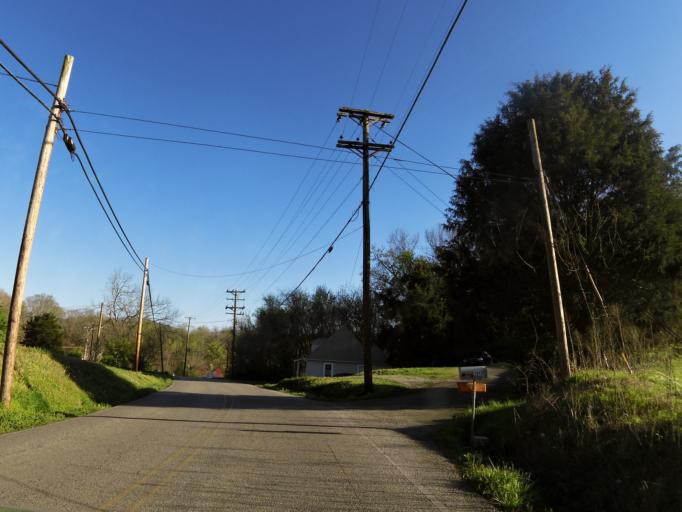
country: US
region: Tennessee
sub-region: Knox County
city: Knoxville
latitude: 35.9750
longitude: -83.8434
